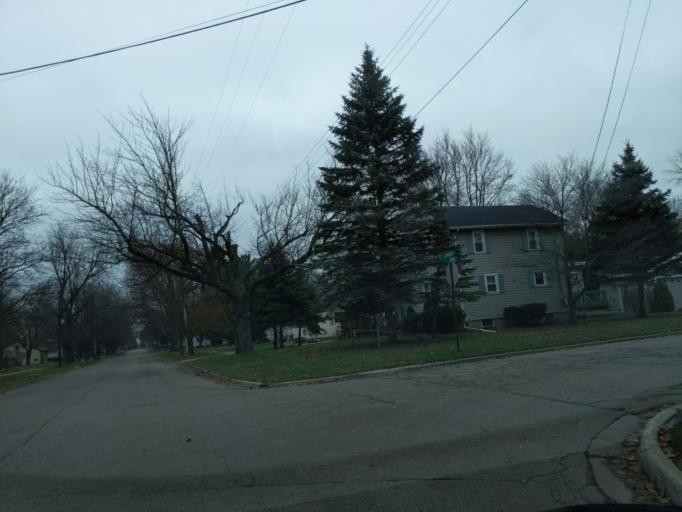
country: US
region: Michigan
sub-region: Clinton County
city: Saint Johns
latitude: 42.9971
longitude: -84.5527
